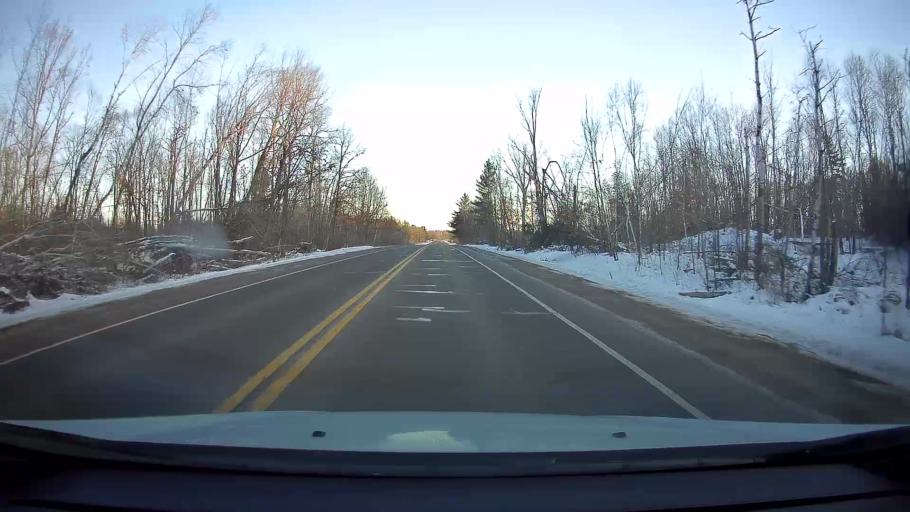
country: US
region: Wisconsin
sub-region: Barron County
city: Turtle Lake
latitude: 45.4223
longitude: -92.1302
